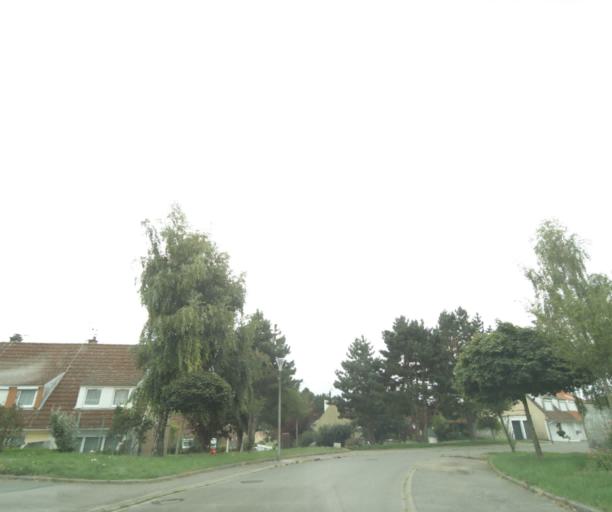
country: FR
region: Nord-Pas-de-Calais
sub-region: Departement du Pas-de-Calais
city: Etaples
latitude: 50.5239
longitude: 1.6455
